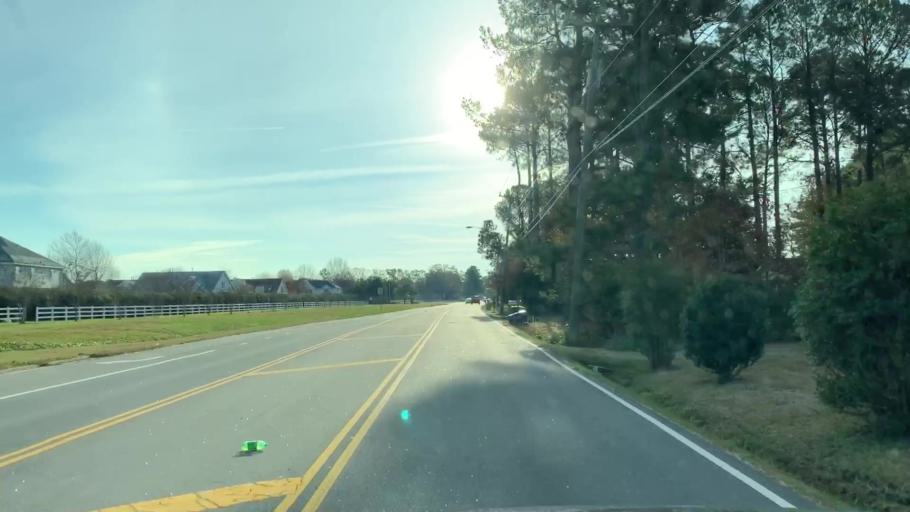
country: US
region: Virginia
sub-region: City of Chesapeake
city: Chesapeake
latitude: 36.7596
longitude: -76.1378
